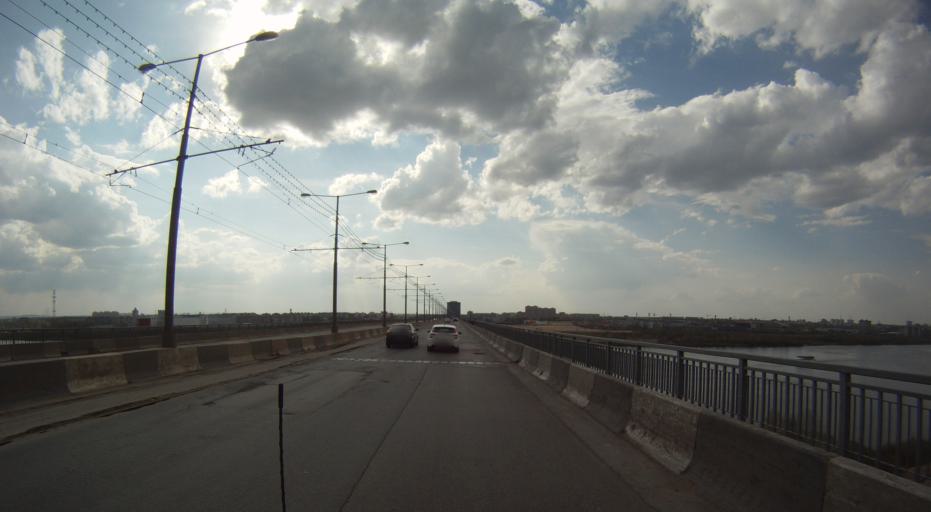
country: RU
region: Nizjnij Novgorod
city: Nizhniy Novgorod
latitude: 56.2989
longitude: 43.9683
